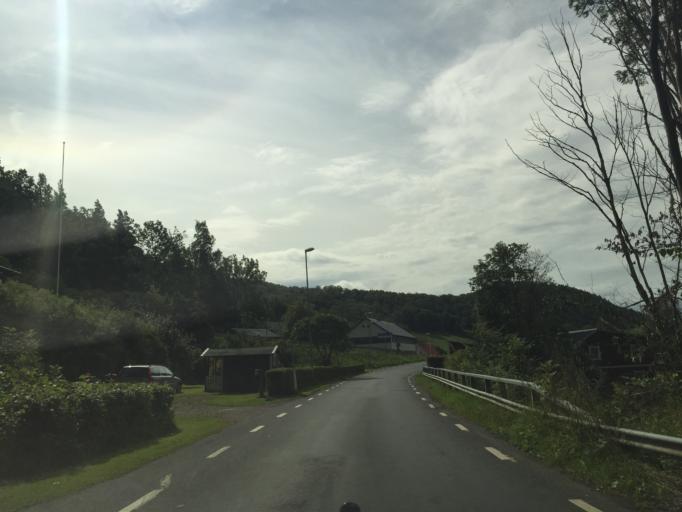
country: SE
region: Joenkoeping
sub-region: Jonkopings Kommun
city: Kaxholmen
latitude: 57.8382
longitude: 14.2722
